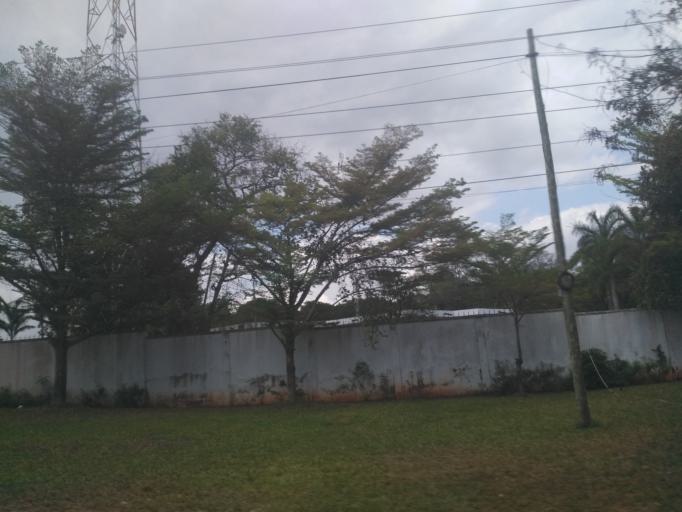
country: TZ
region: Dar es Salaam
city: Magomeni
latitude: -6.7626
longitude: 39.2787
